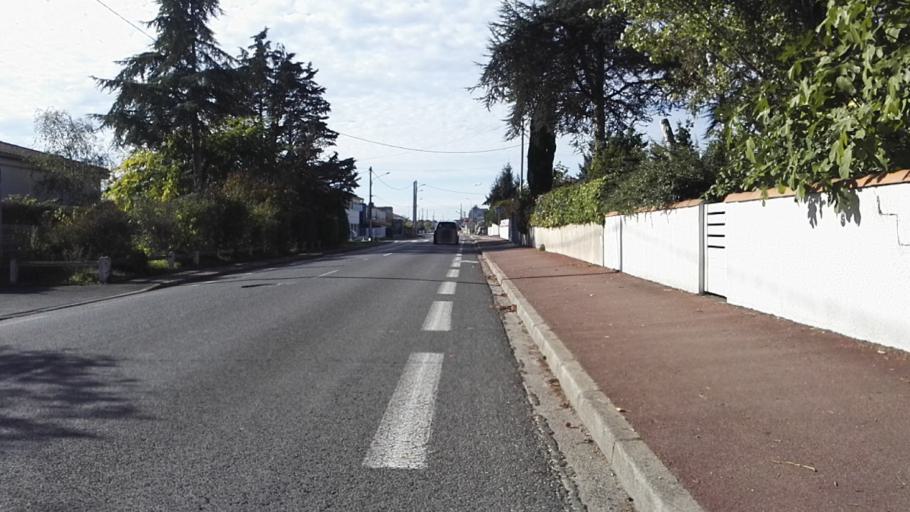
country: FR
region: Aquitaine
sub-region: Departement de la Gironde
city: Merignac
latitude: 44.8563
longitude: -0.6408
